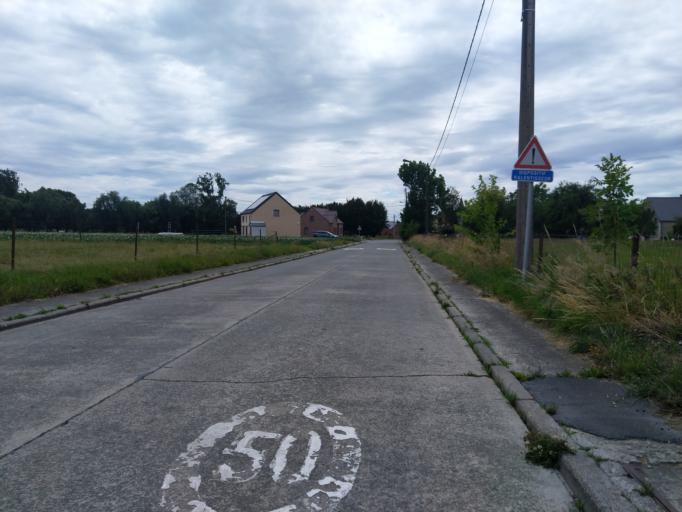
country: BE
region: Wallonia
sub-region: Province du Hainaut
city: Beloeil
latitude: 50.5467
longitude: 3.7602
